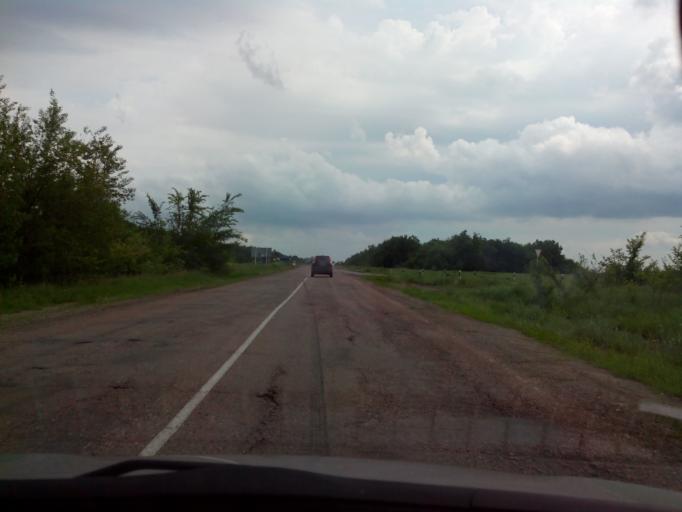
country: RU
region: Volgograd
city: Mikhaylovka
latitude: 49.9812
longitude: 43.0795
